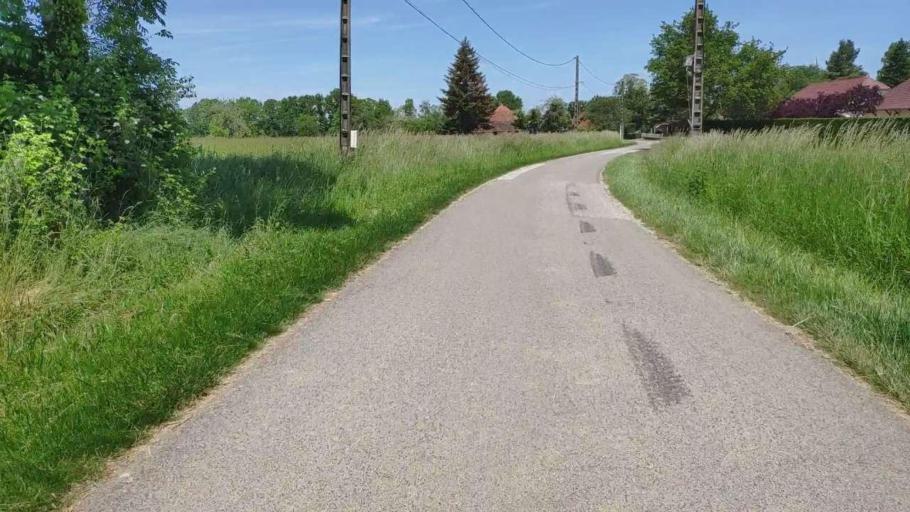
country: FR
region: Franche-Comte
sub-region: Departement du Jura
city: Bletterans
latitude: 46.7917
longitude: 5.3761
